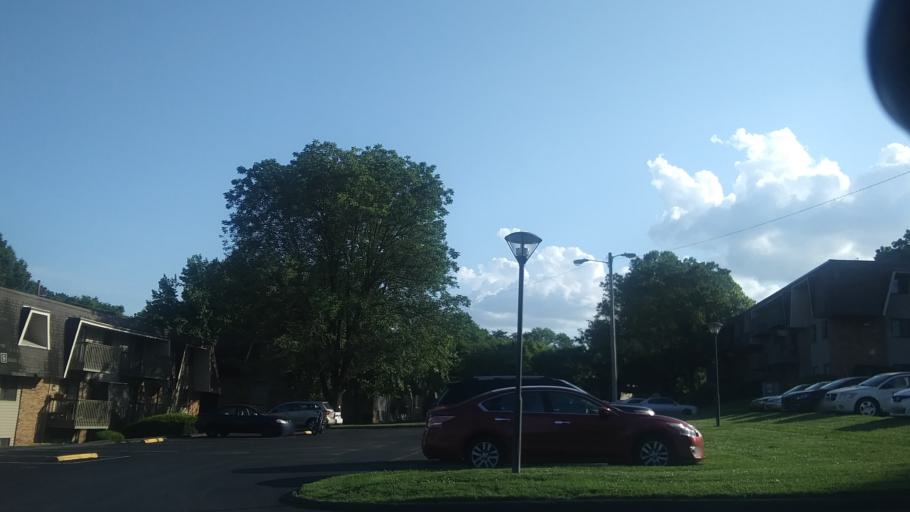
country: US
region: Tennessee
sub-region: Davidson County
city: Oak Hill
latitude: 36.0808
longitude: -86.7036
